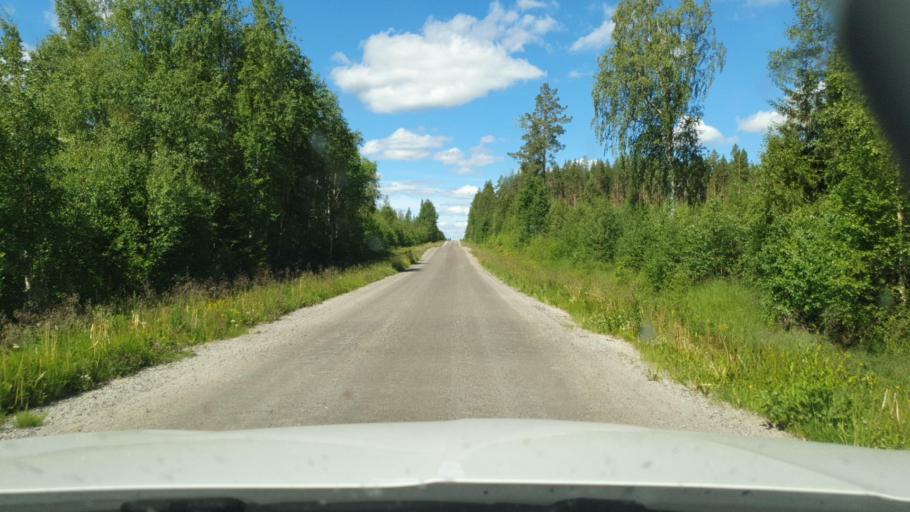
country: SE
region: Vaesterbotten
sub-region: Skelleftea Kommun
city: Backa
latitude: 65.1430
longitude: 21.1749
